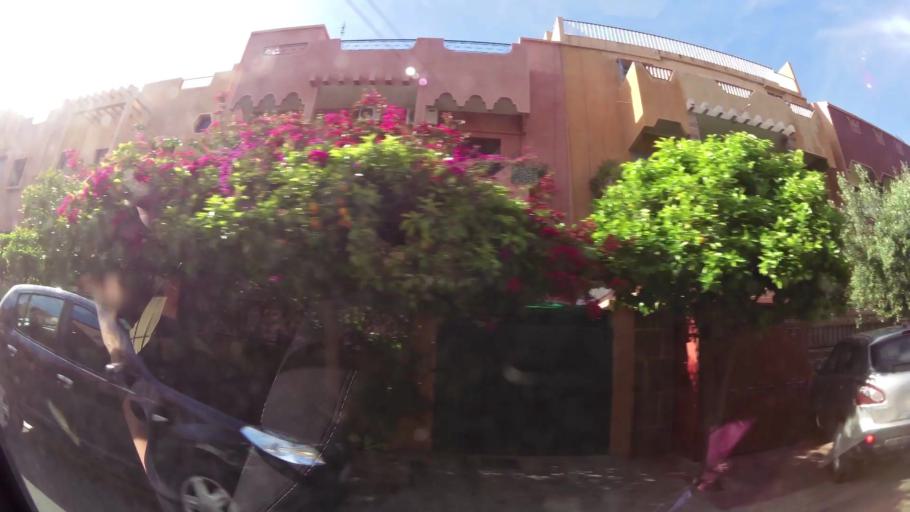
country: MA
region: Marrakech-Tensift-Al Haouz
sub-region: Marrakech
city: Marrakesh
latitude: 31.6531
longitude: -8.0070
